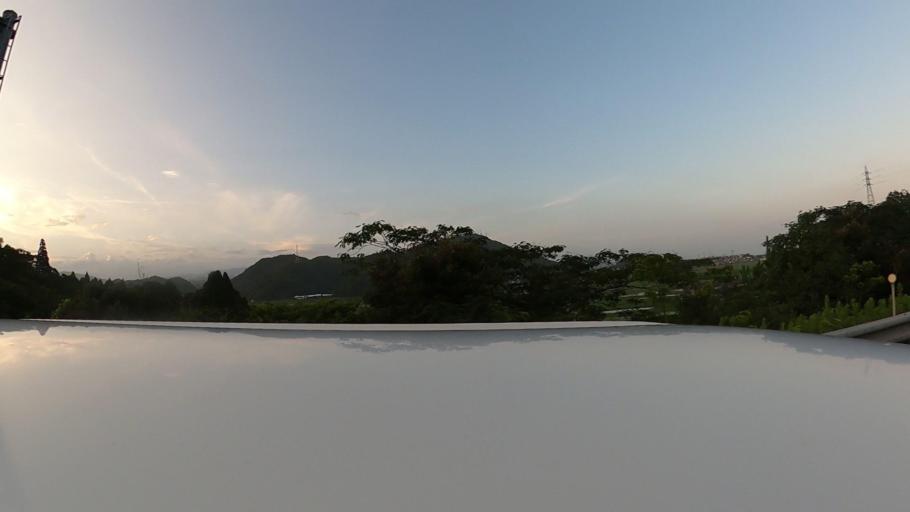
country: JP
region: Miyazaki
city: Nobeoka
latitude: 32.5429
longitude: 131.6516
